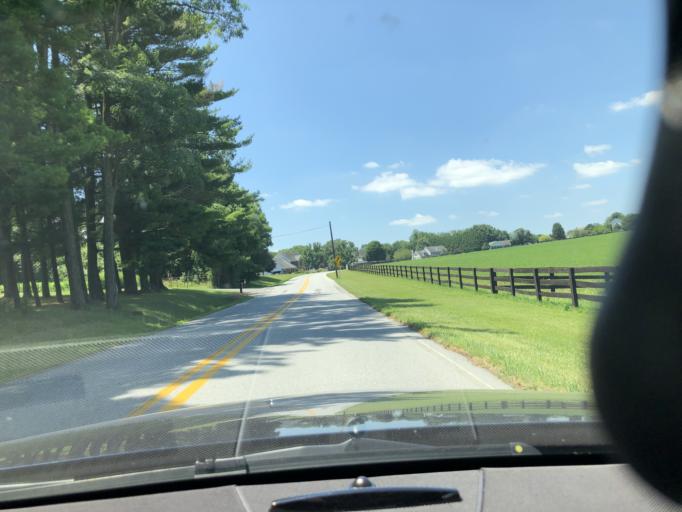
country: US
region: Maryland
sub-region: Carroll County
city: Westminster
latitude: 39.5081
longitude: -76.9347
